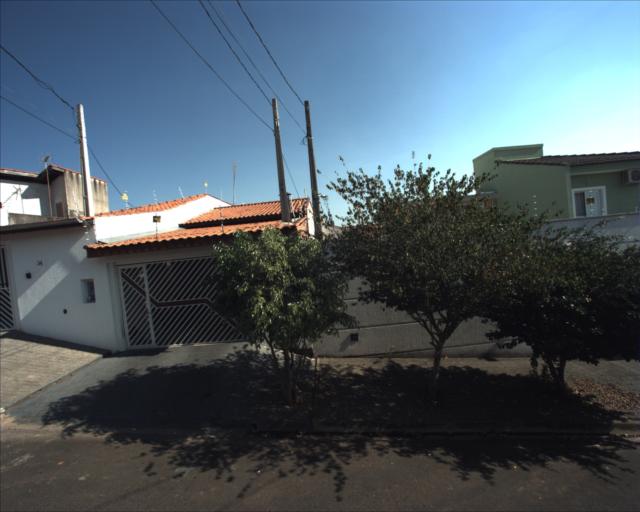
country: BR
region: Sao Paulo
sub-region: Sorocaba
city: Sorocaba
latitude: -23.4992
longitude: -47.4254
